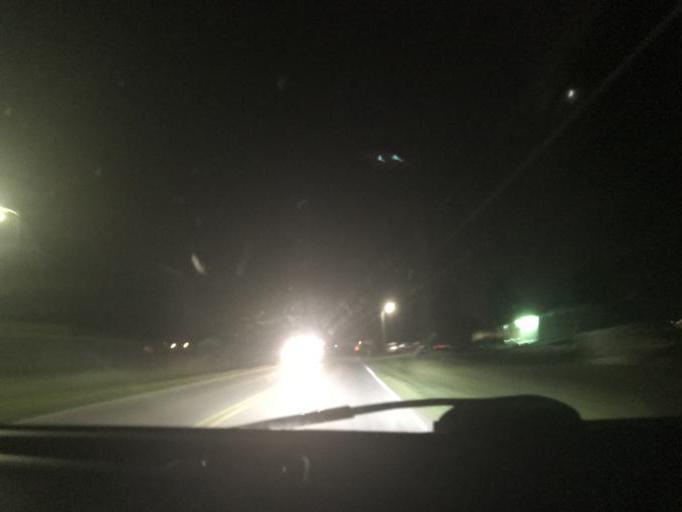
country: US
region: South Carolina
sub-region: Cherokee County
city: East Gaffney
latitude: 35.1063
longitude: -81.6535
